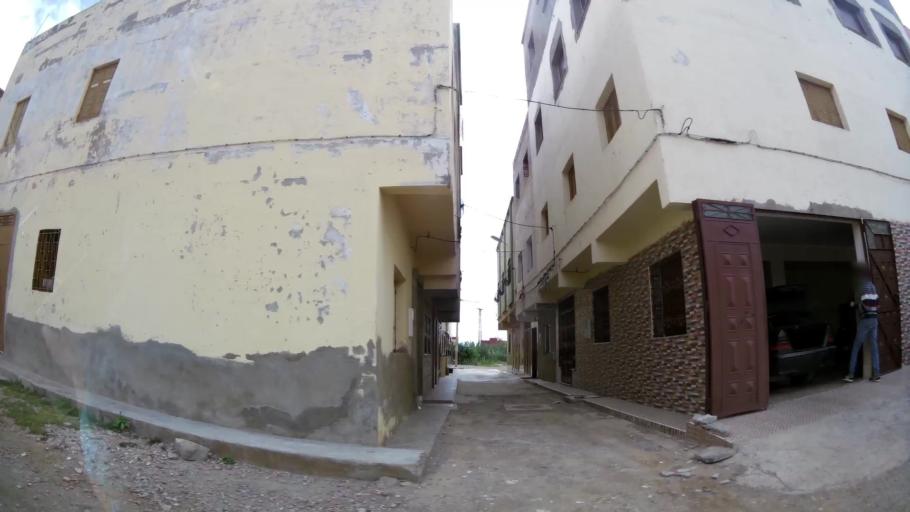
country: MA
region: Oriental
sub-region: Nador
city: Nador
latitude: 35.1594
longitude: -2.9263
